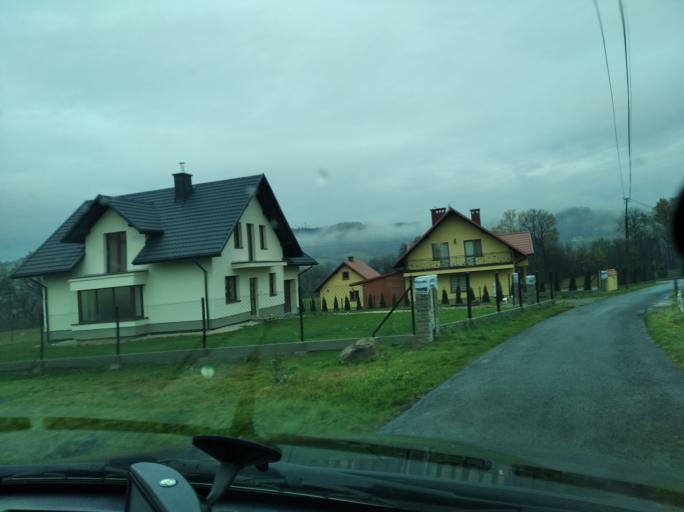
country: PL
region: Subcarpathian Voivodeship
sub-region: Powiat strzyzowski
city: Babica
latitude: 49.9296
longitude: 21.8796
